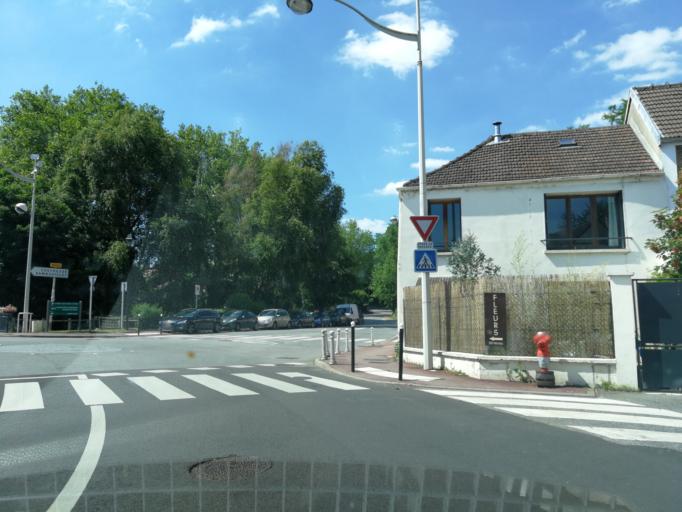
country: FR
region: Ile-de-France
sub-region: Departement des Yvelines
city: Saint-Remy-les-Chevreuse
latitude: 48.7071
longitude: 2.0715
